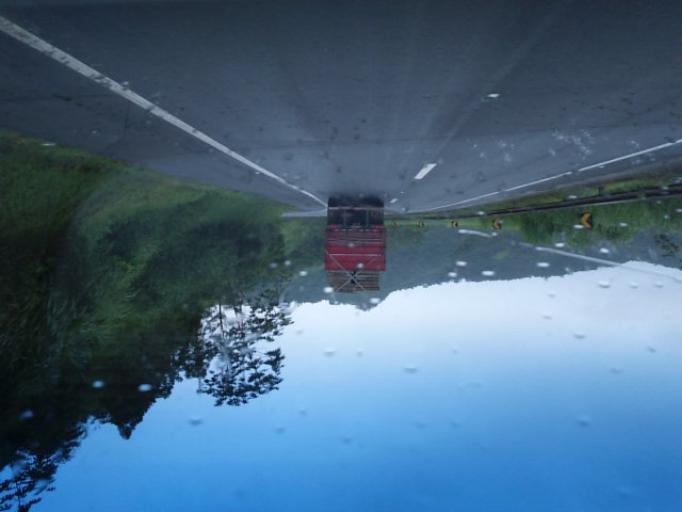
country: BR
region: Sao Paulo
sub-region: Cajati
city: Cajati
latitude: -24.7823
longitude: -48.2041
